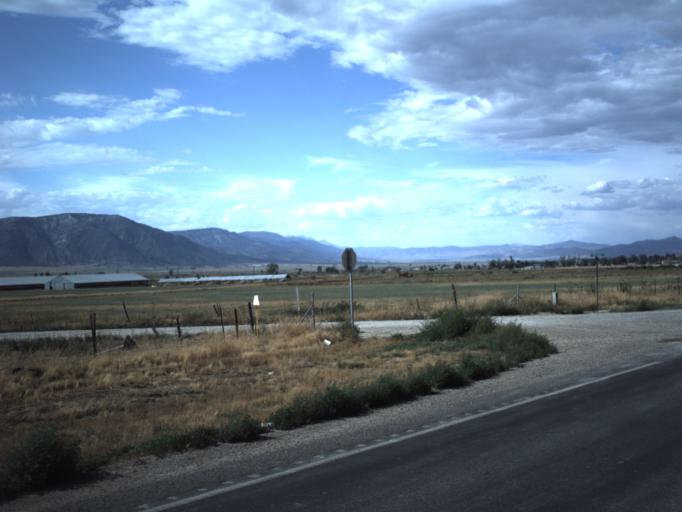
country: US
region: Utah
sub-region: Sanpete County
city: Ephraim
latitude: 39.3372
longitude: -111.5960
